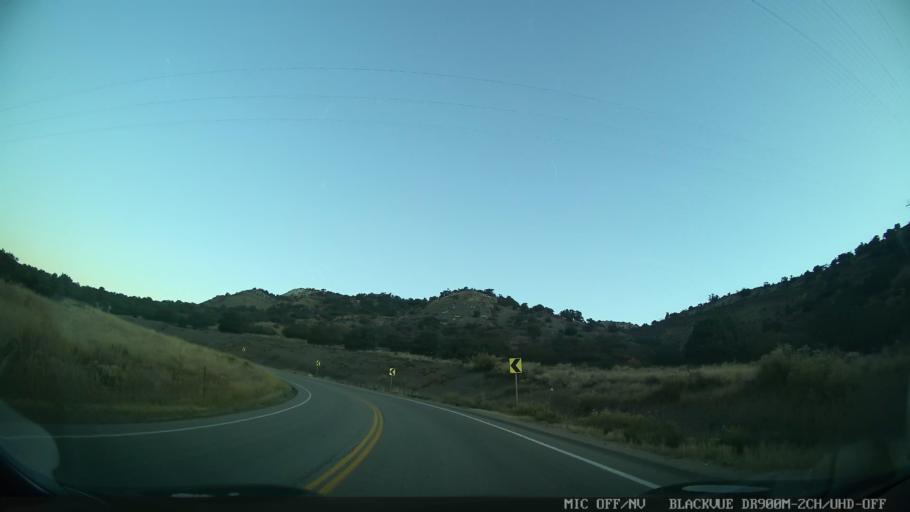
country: US
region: Colorado
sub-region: Eagle County
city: Edwards
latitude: 39.7033
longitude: -106.6776
